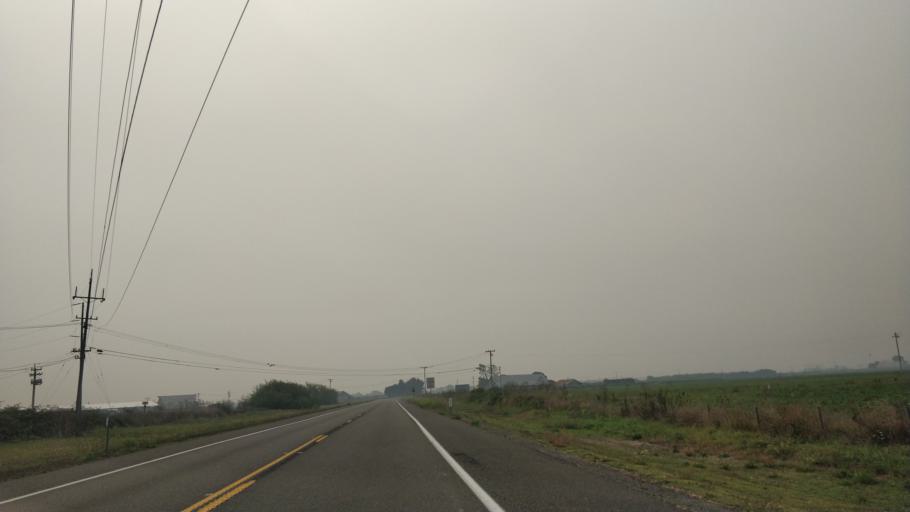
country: US
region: California
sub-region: Humboldt County
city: Fortuna
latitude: 40.6039
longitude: -124.2102
